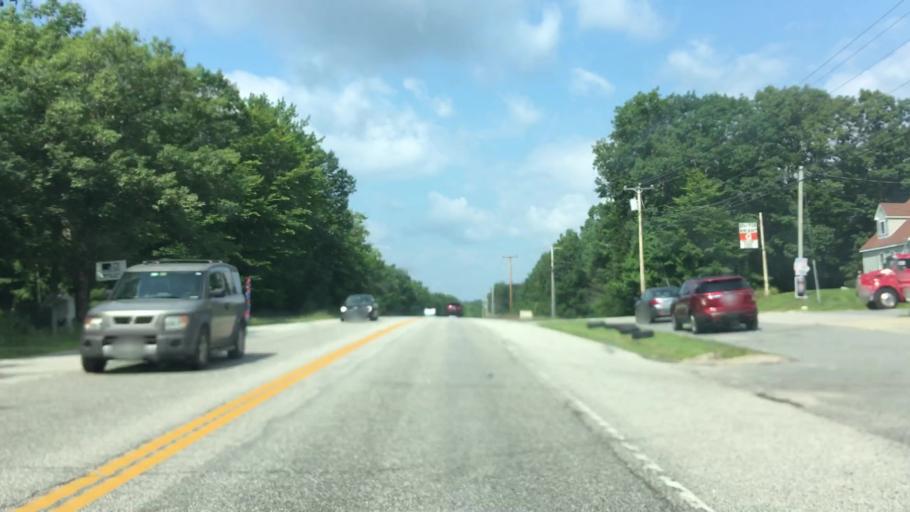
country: US
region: Maine
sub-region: Cumberland County
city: Raymond
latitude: 43.9092
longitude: -70.4984
